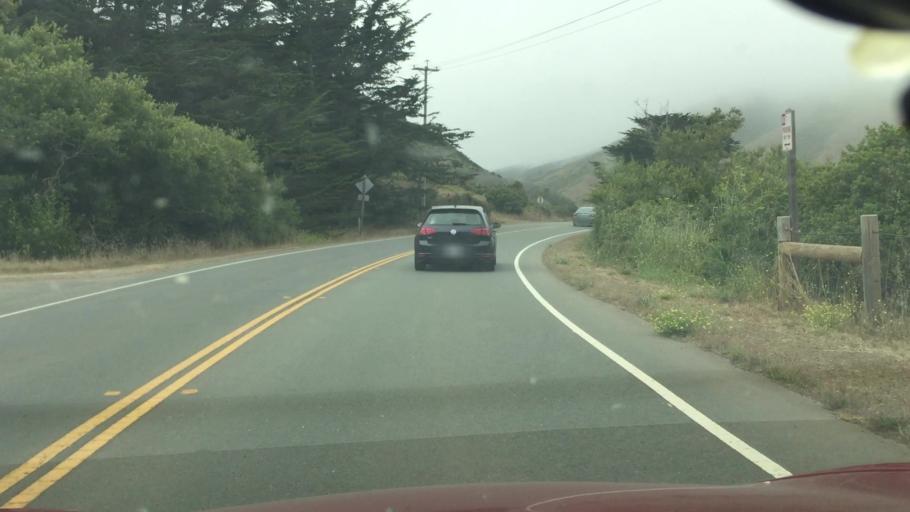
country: US
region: California
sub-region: Marin County
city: Marin City
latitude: 37.8319
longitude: -122.5158
